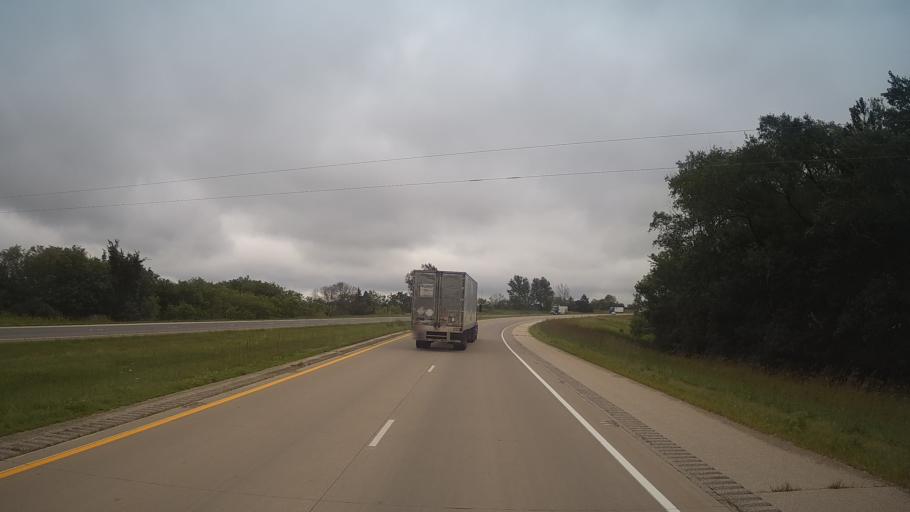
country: US
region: Minnesota
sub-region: Winona County
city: Saint Charles
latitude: 43.9370
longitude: -91.9797
